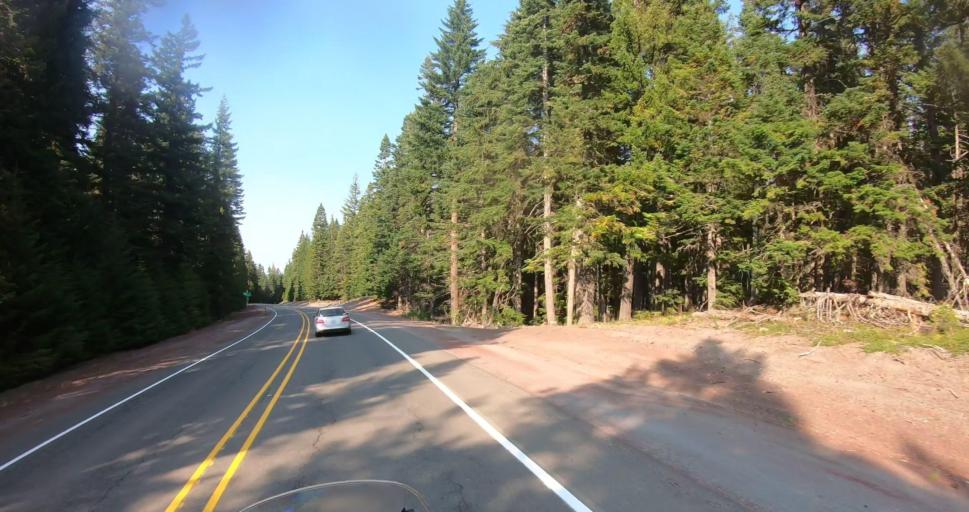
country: US
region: Oregon
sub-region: Hood River County
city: Odell
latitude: 45.3723
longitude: -121.5667
